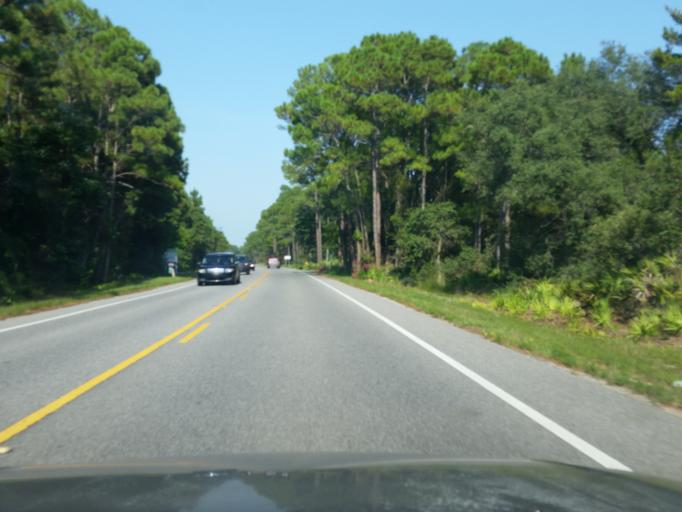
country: US
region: Alabama
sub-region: Baldwin County
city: Gulf Shores
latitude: 30.2386
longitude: -87.8658
